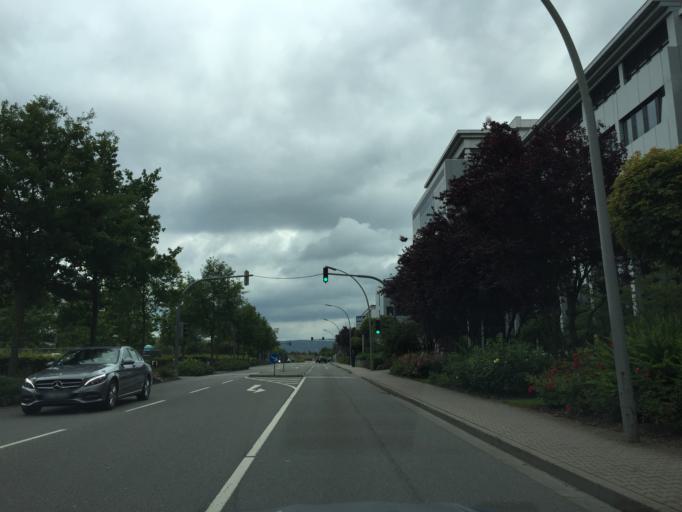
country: DE
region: Baden-Wuerttemberg
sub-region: Karlsruhe Region
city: Walldorf
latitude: 49.2940
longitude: 8.6435
